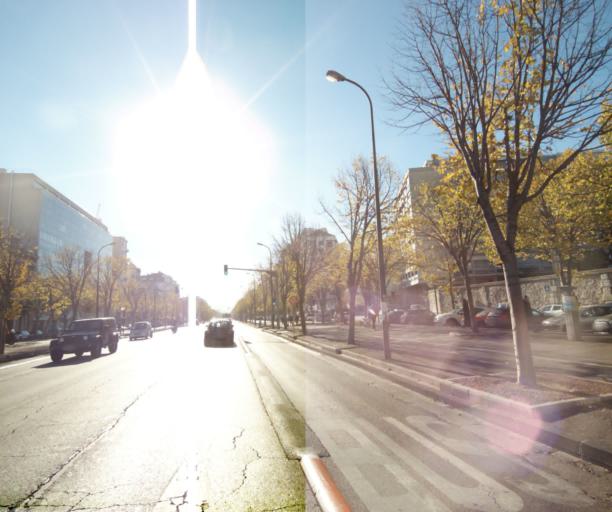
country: FR
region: Provence-Alpes-Cote d'Azur
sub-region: Departement des Bouches-du-Rhone
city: Marseille 08
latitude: 43.2792
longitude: 5.3875
